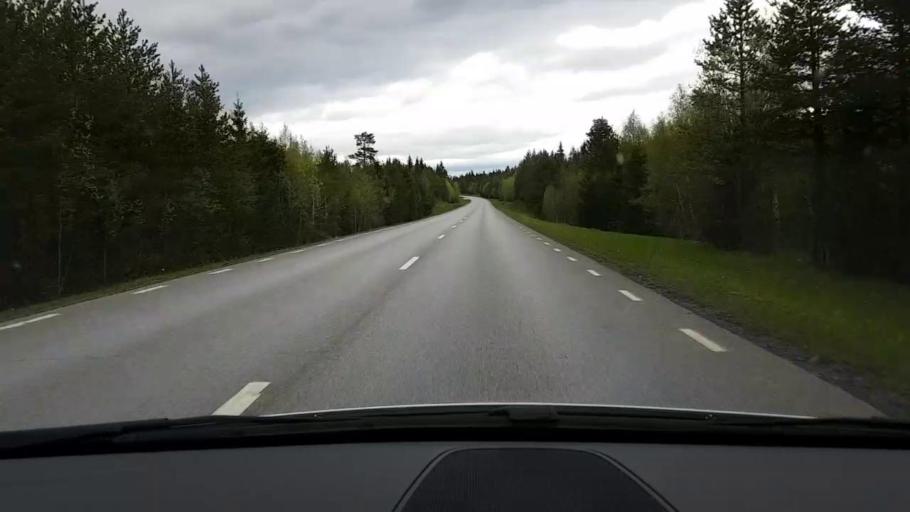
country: SE
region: Jaemtland
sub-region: Krokoms Kommun
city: Valla
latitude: 63.2936
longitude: 13.9268
